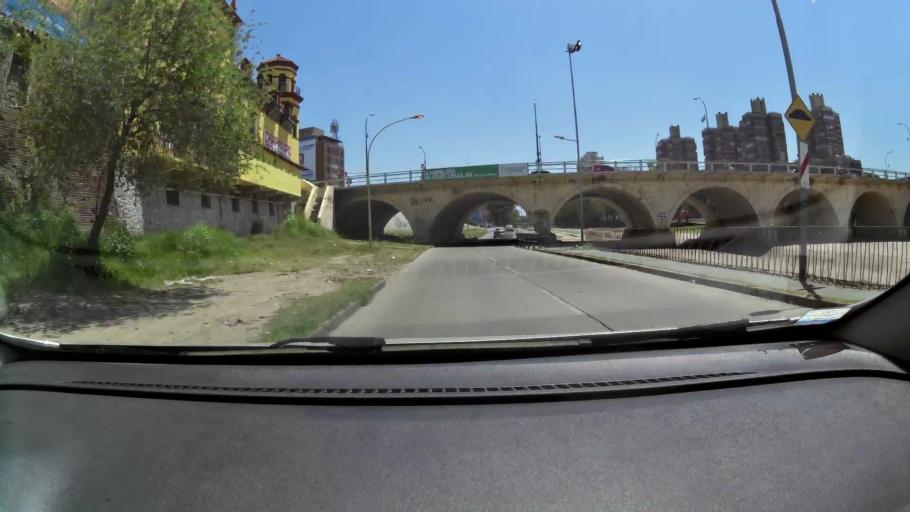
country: AR
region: Cordoba
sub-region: Departamento de Capital
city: Cordoba
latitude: -31.4063
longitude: -64.1934
